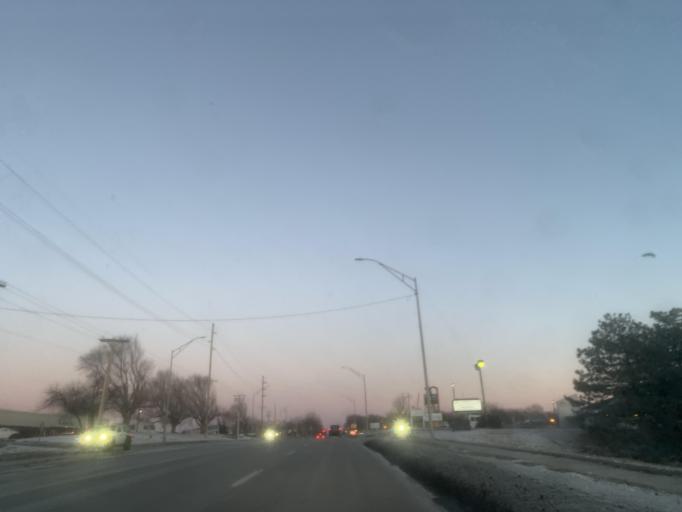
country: US
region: Nebraska
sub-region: Douglas County
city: Ralston
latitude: 41.2053
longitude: -96.0847
